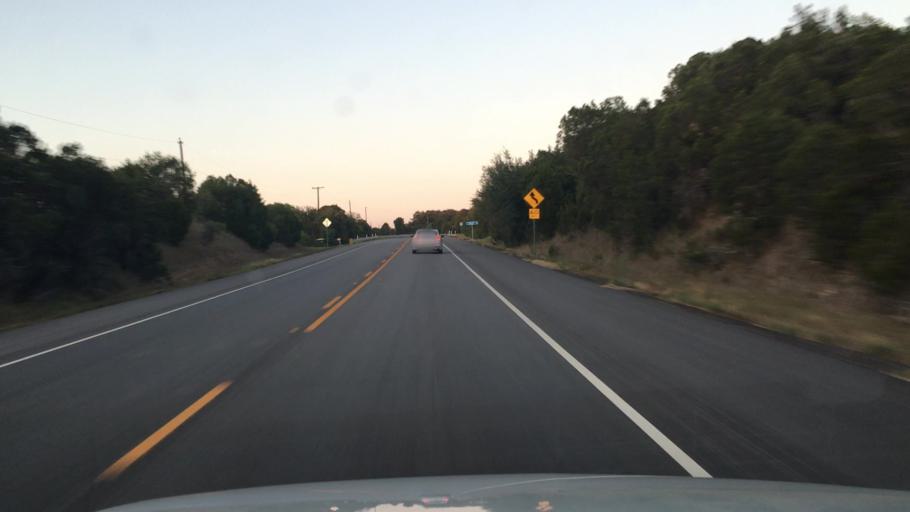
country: US
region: Texas
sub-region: Somervell County
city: Glen Rose
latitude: 32.1940
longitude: -97.8160
